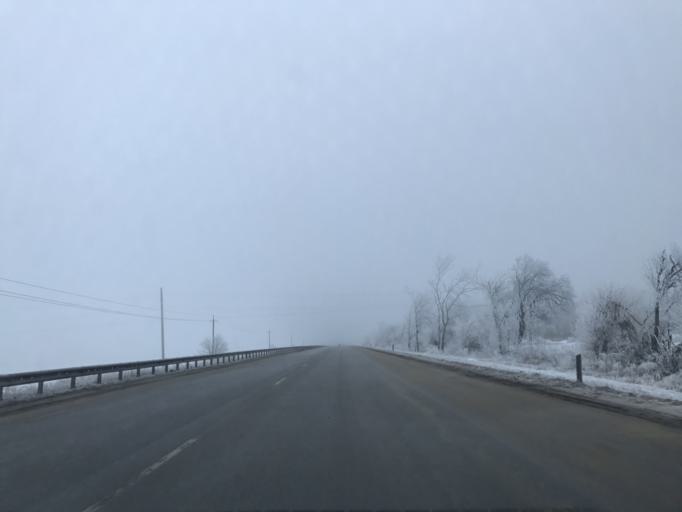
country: RU
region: Rostov
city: Grushevskaya
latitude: 47.3787
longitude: 39.8691
